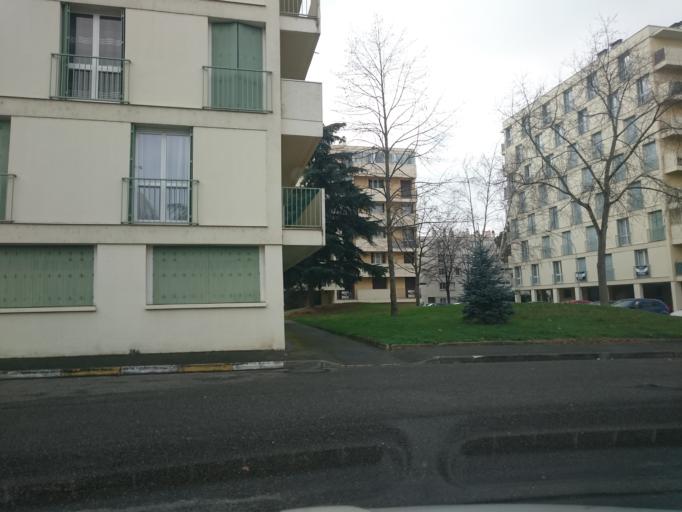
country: FR
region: Midi-Pyrenees
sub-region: Departement de la Haute-Garonne
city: Colomiers
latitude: 43.6103
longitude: 1.3279
